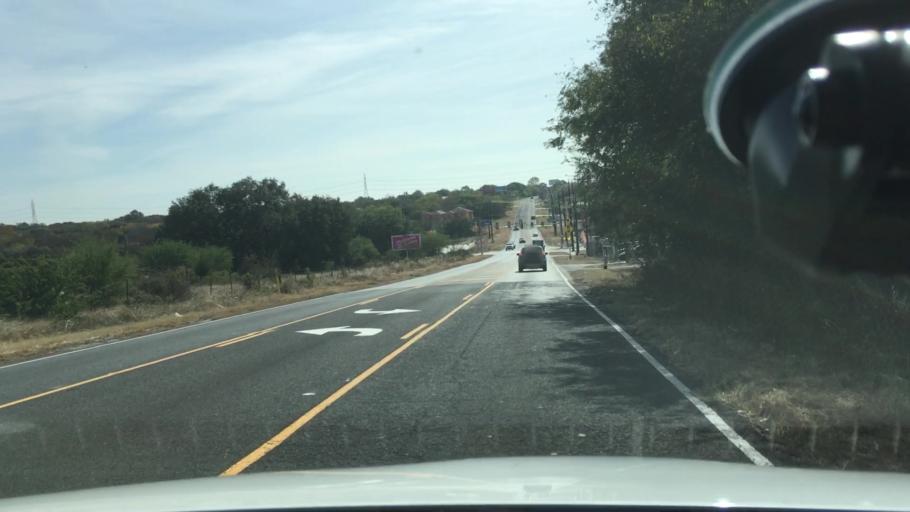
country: US
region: Texas
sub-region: Bexar County
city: Hollywood Park
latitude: 29.5809
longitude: -98.4211
